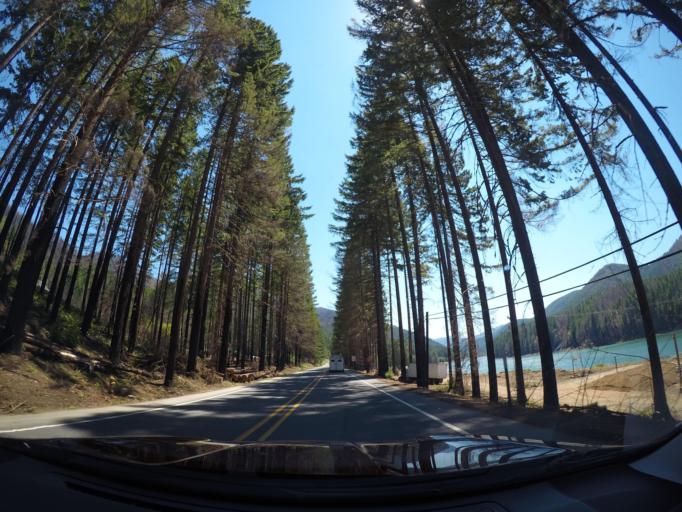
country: US
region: Oregon
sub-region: Linn County
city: Mill City
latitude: 44.7294
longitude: -122.1457
